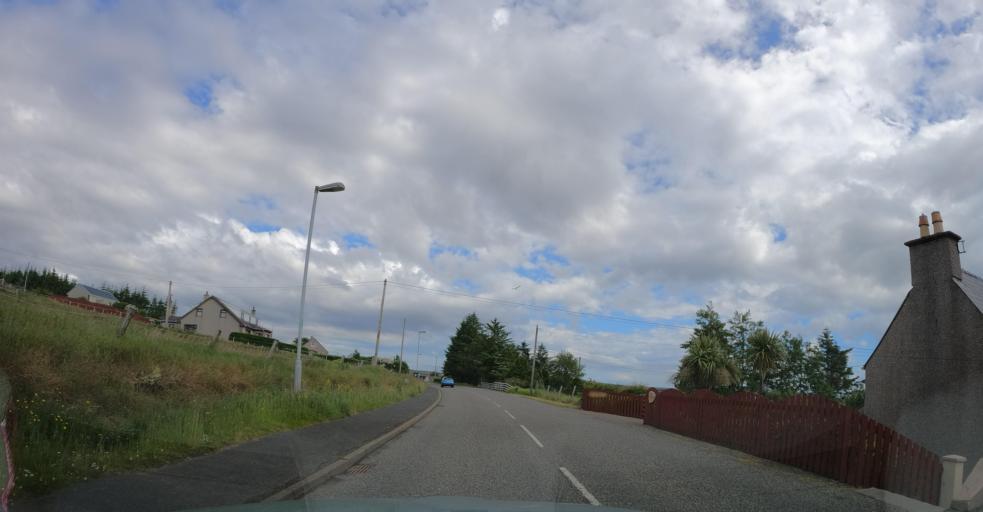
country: GB
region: Scotland
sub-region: Eilean Siar
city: Isle of Lewis
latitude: 58.2383
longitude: -6.3878
